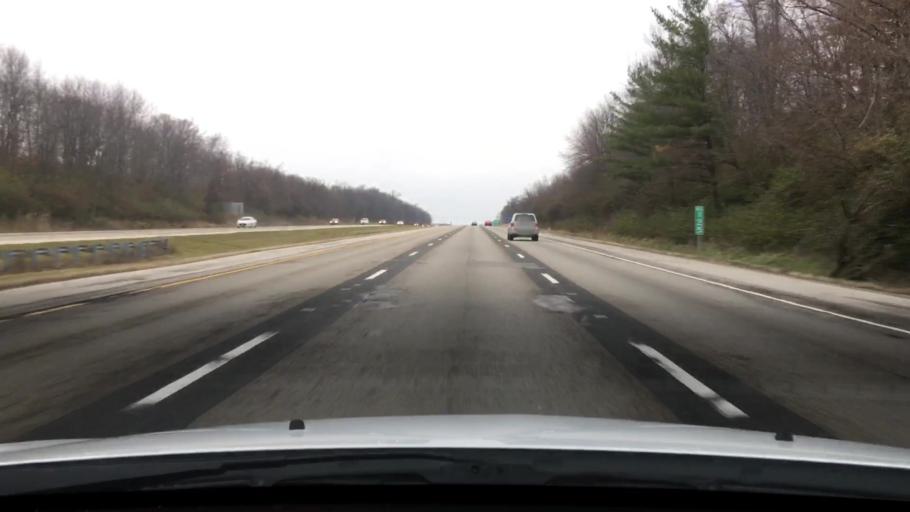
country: US
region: Illinois
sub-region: Logan County
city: Lincoln
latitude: 40.1471
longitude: -89.4171
